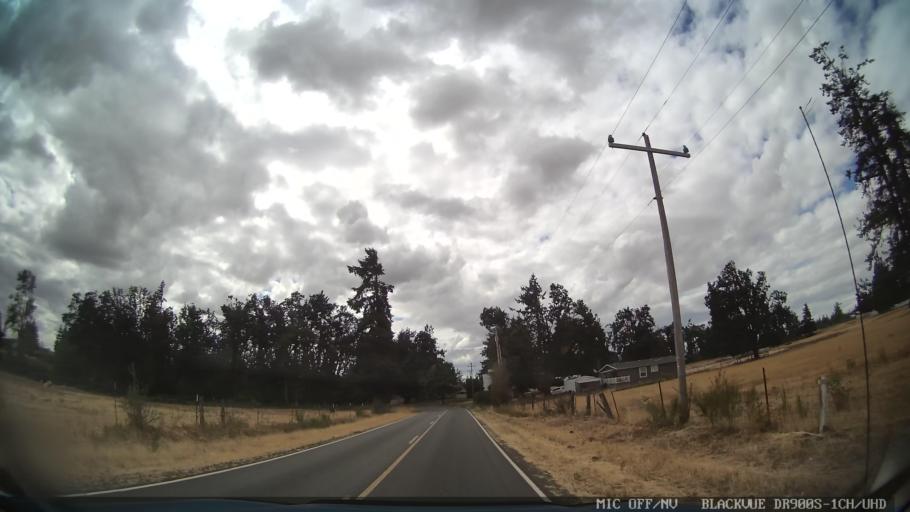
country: US
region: Oregon
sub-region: Marion County
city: Sublimity
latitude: 44.8443
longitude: -122.7723
